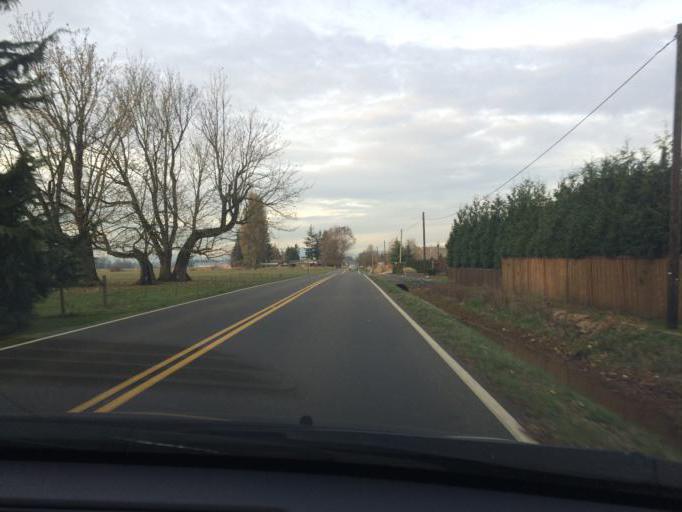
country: US
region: Washington
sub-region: Whatcom County
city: Lynden
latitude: 48.9587
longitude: -122.4633
